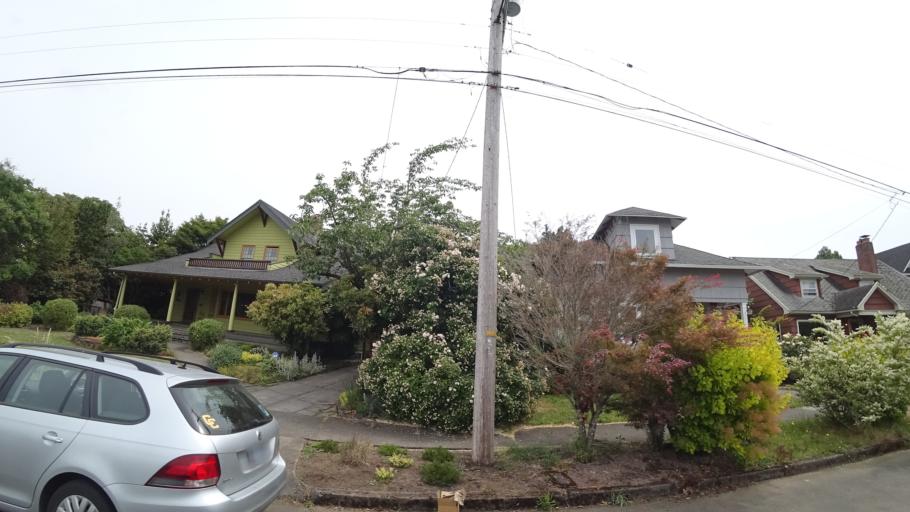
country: US
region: Oregon
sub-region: Multnomah County
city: Portland
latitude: 45.5692
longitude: -122.6997
